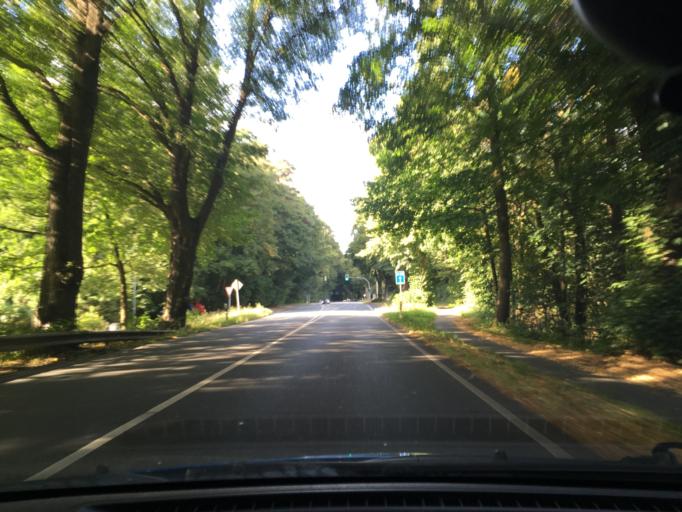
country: DE
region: Lower Saxony
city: Seevetal
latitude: 53.4107
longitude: 9.9267
